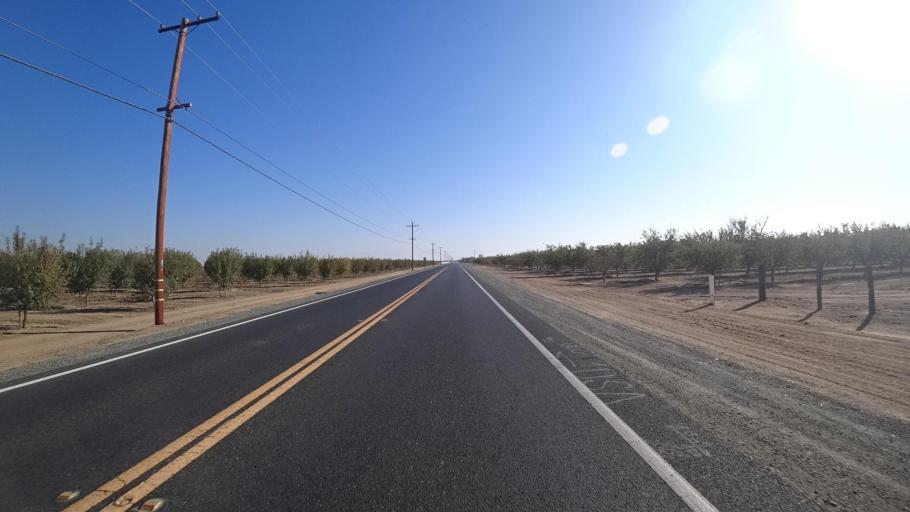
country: US
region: California
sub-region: Kern County
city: Delano
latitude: 35.7615
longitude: -119.2180
